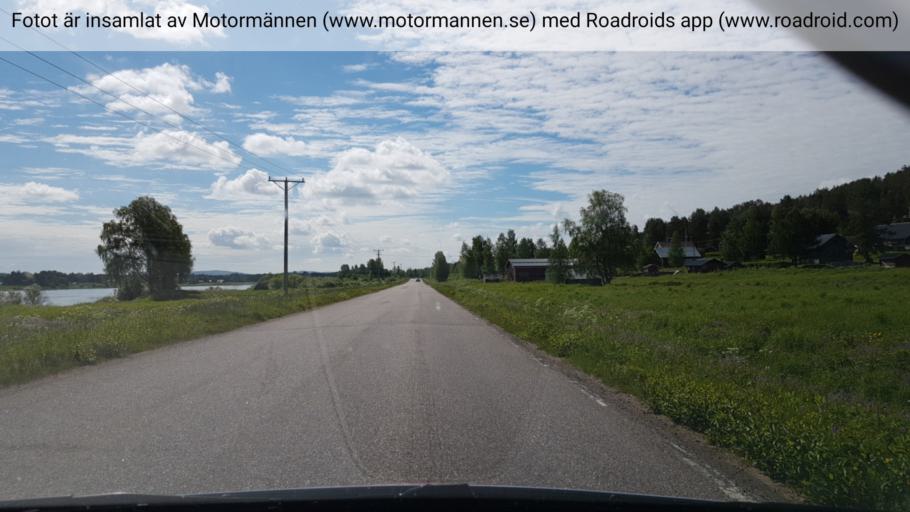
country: FI
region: Lapland
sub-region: Torniolaakso
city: Pello
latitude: 66.6494
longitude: 23.8621
